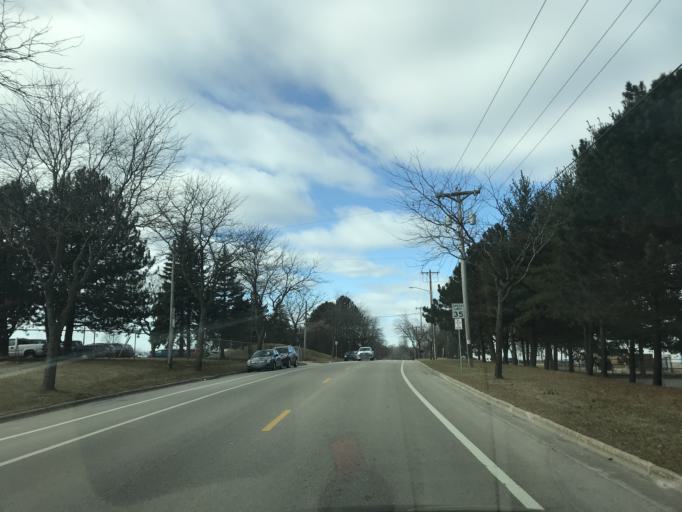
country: US
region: Wisconsin
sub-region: Dane County
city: Monona
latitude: 43.1139
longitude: -89.3015
